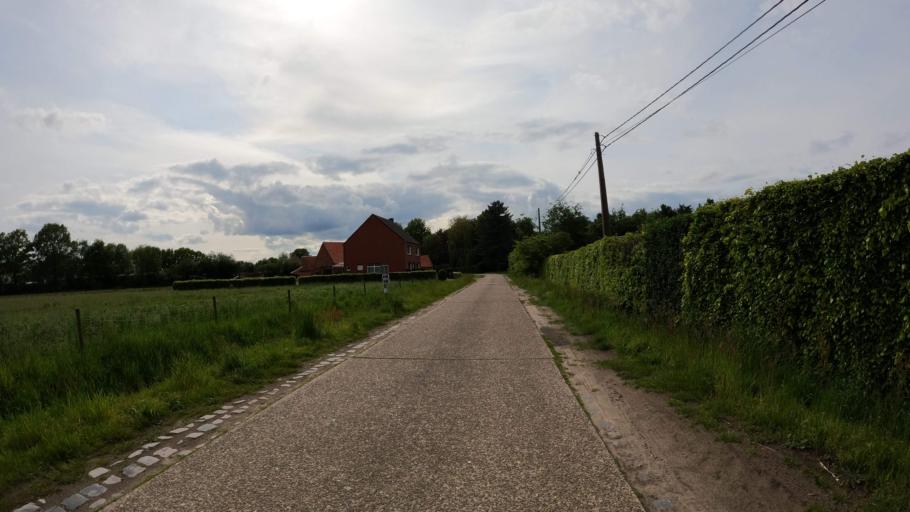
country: BE
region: Flanders
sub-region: Provincie Antwerpen
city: Vosselaar
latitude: 51.2635
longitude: 4.8949
